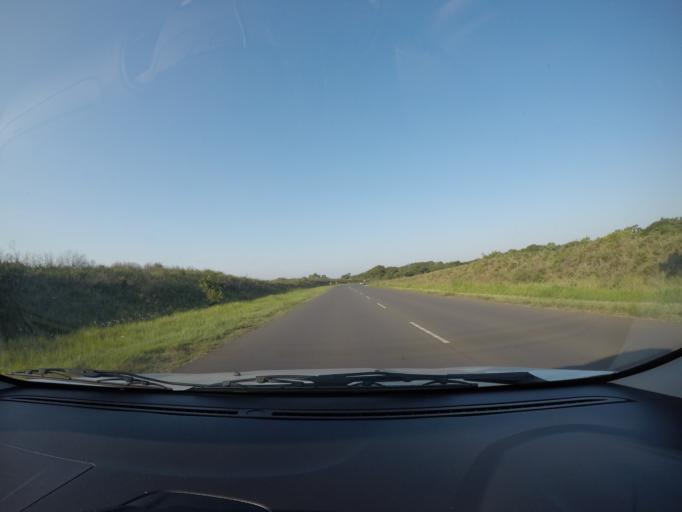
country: ZA
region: KwaZulu-Natal
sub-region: uThungulu District Municipality
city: Richards Bay
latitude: -28.7490
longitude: 32.0118
